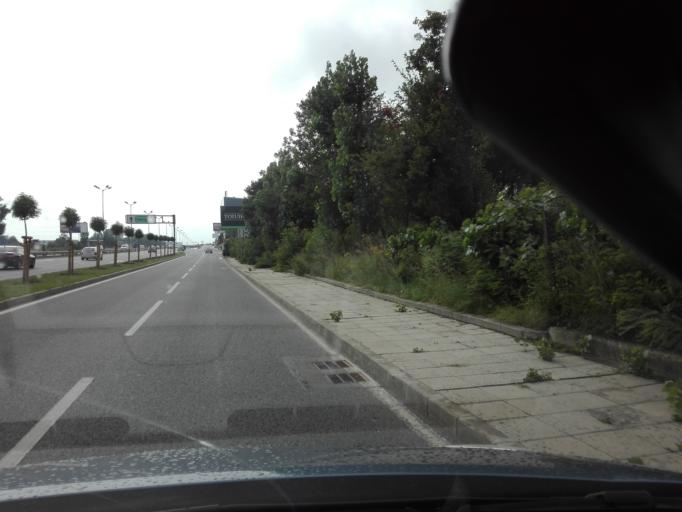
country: BG
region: Sofia-Capital
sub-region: Stolichna Obshtina
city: Sofia
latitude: 42.6443
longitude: 23.3053
